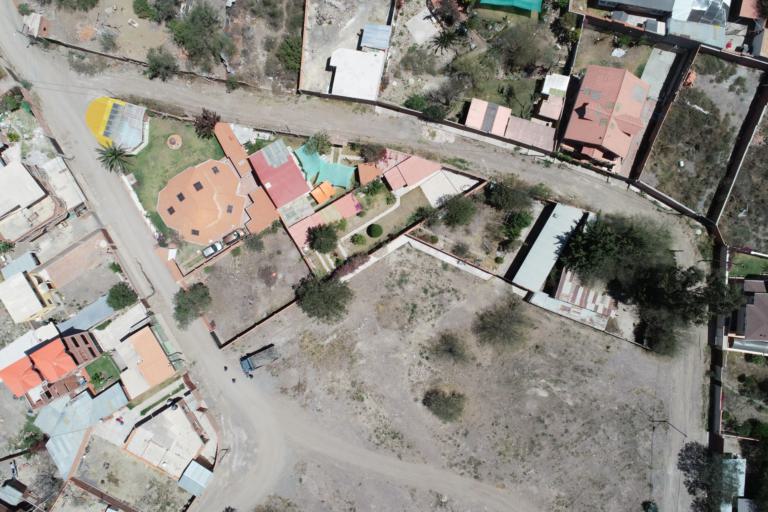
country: BO
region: La Paz
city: La Paz
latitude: -16.6449
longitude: -68.0429
